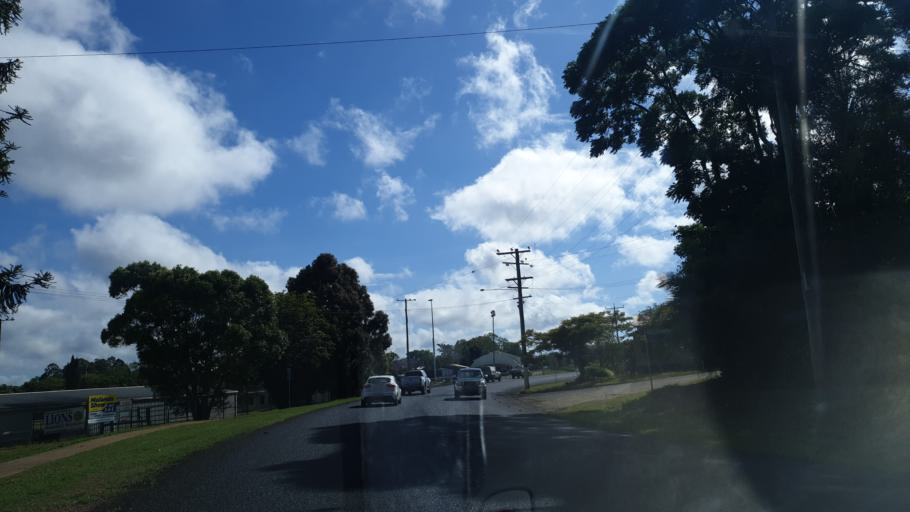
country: AU
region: Queensland
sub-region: Tablelands
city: Atherton
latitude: -17.3525
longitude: 145.5893
